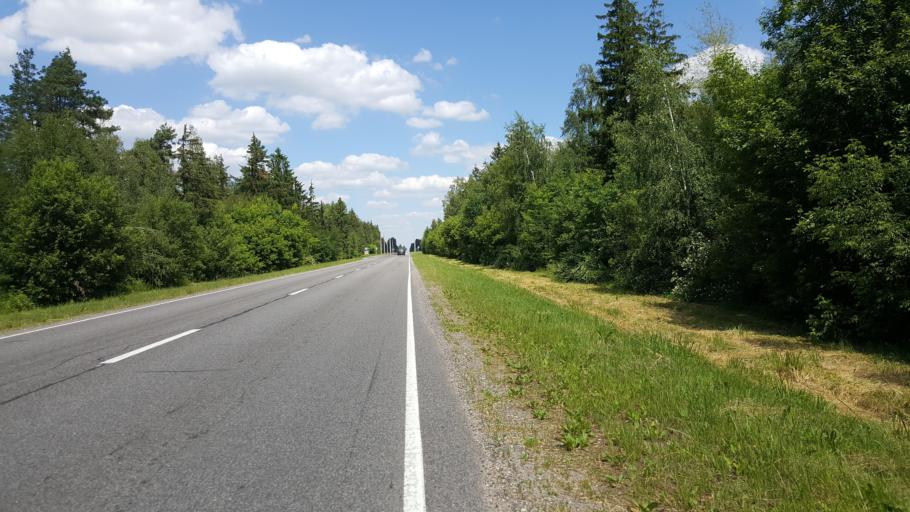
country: BY
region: Brest
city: Kamyanyets
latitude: 52.4417
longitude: 23.7847
